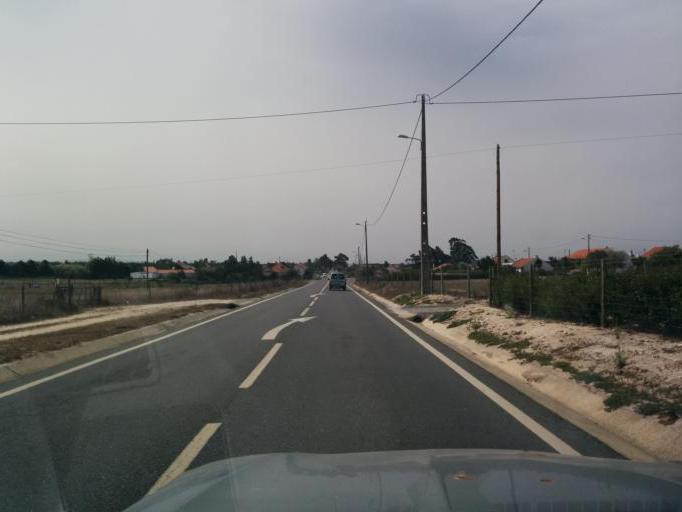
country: PT
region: Beja
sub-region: Odemira
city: Vila Nova de Milfontes
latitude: 37.6582
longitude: -8.7595
